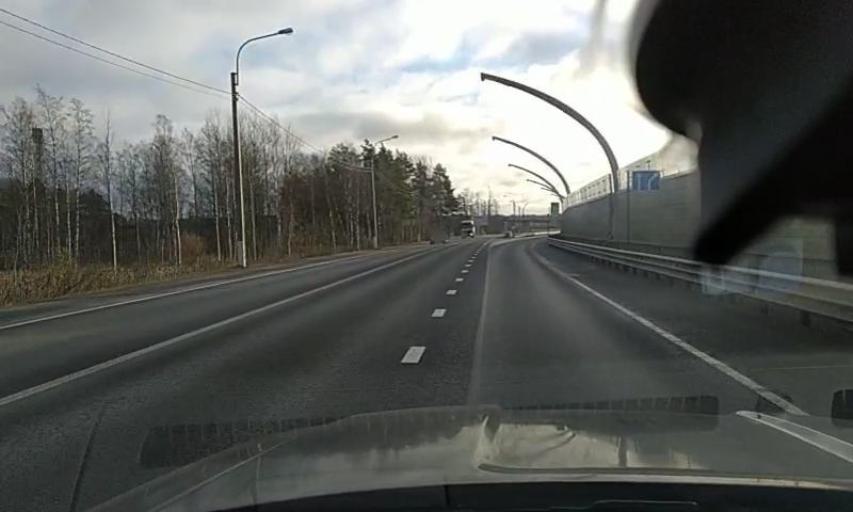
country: RU
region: St.-Petersburg
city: Solnechnoye
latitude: 60.1531
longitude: 29.9673
